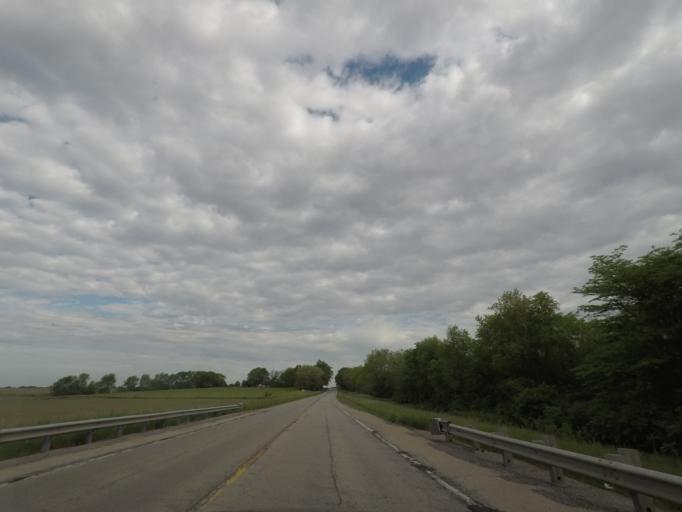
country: US
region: Illinois
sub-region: Logan County
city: Lincoln
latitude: 40.1200
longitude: -89.3356
